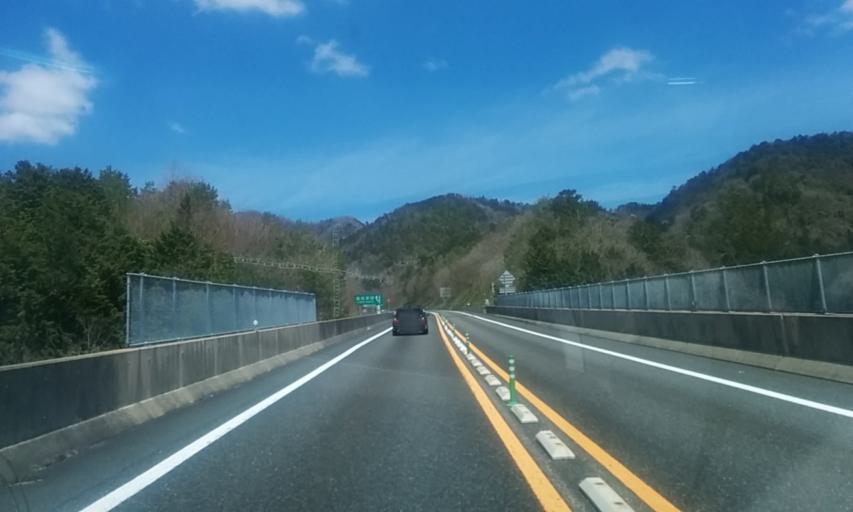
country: JP
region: Kyoto
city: Ayabe
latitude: 35.3880
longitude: 135.2413
